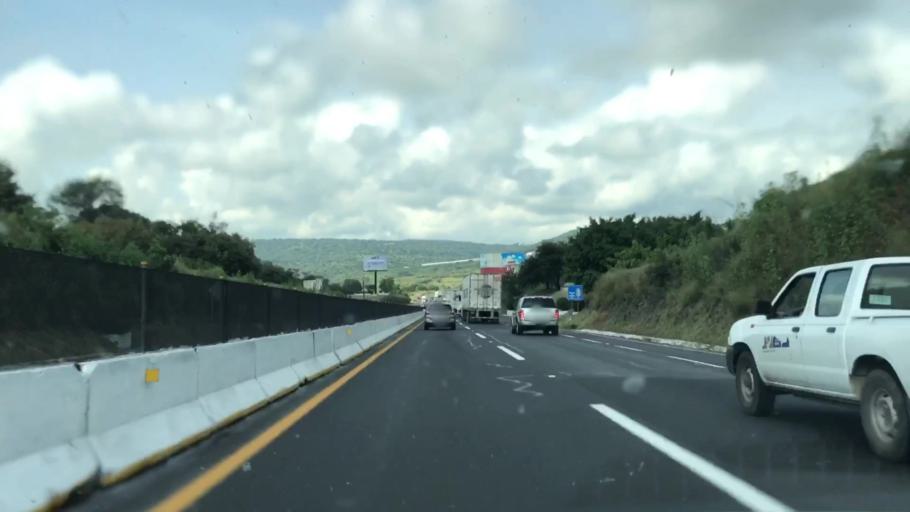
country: MX
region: Jalisco
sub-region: Tonala
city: Mismaloya (Fraccionamiento Pedregal de Santa Martha)
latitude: 20.6028
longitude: -103.1433
